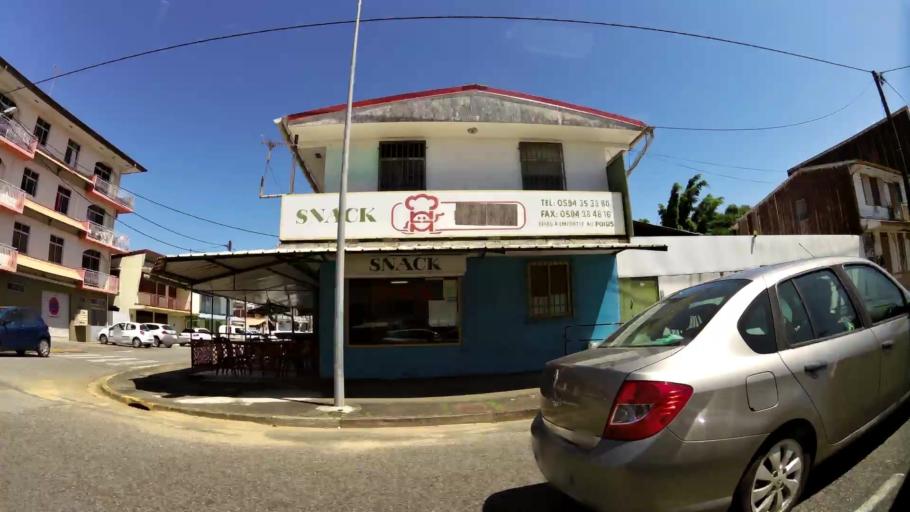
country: GF
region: Guyane
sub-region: Guyane
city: Cayenne
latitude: 4.9432
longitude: -52.3245
